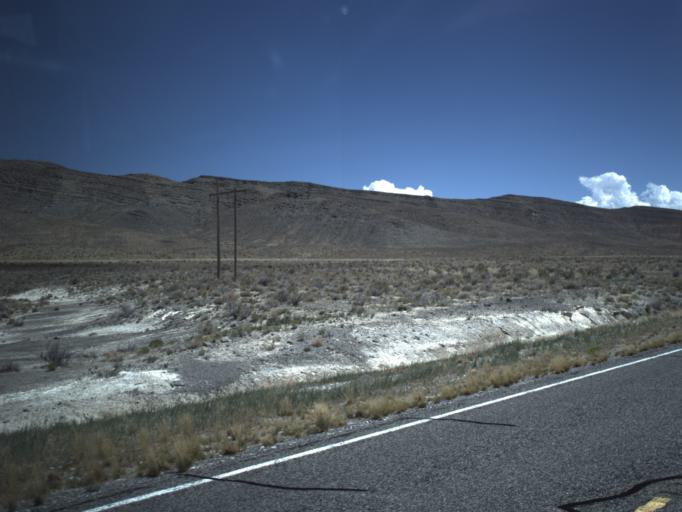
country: US
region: Utah
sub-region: Beaver County
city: Milford
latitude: 39.0354
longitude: -113.3911
